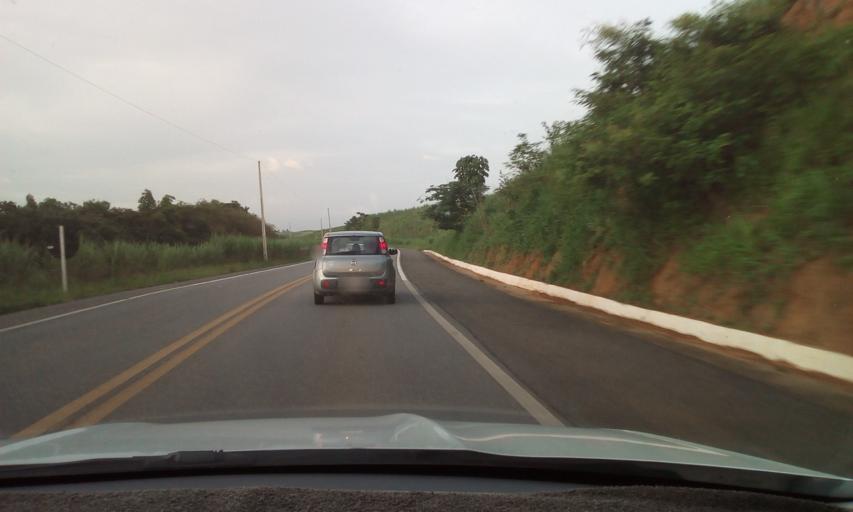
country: BR
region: Pernambuco
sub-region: Vicencia
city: Vicencia
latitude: -7.6393
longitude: -35.2541
